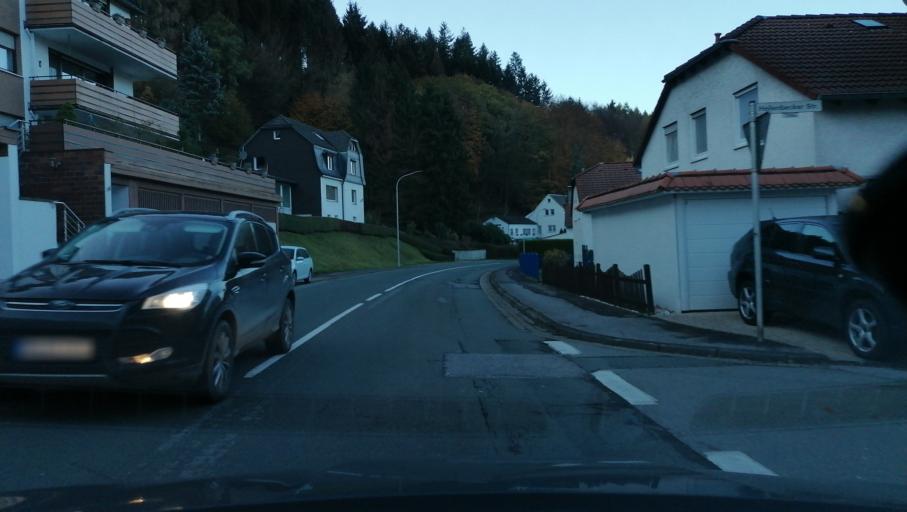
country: DE
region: North Rhine-Westphalia
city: Ennepetal
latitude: 51.2862
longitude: 7.3396
